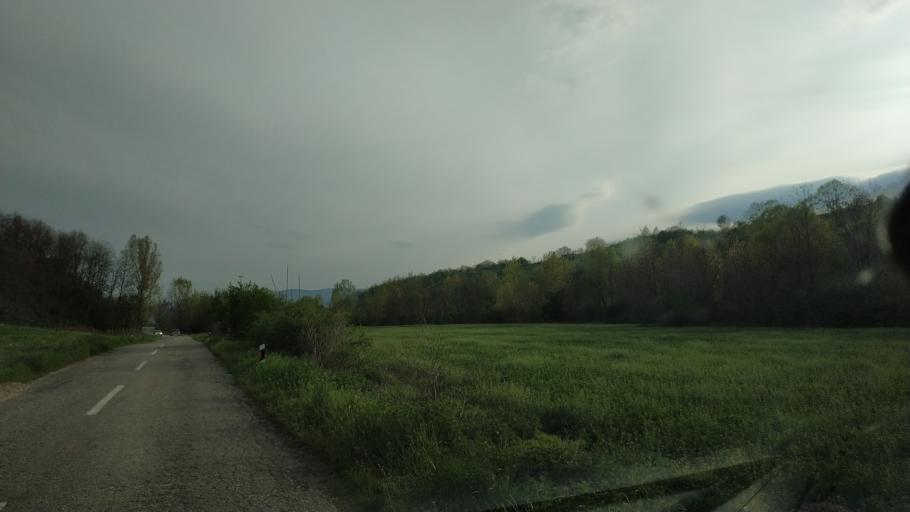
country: RS
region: Central Serbia
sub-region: Nisavski Okrug
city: Aleksinac
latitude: 43.4596
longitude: 21.8019
